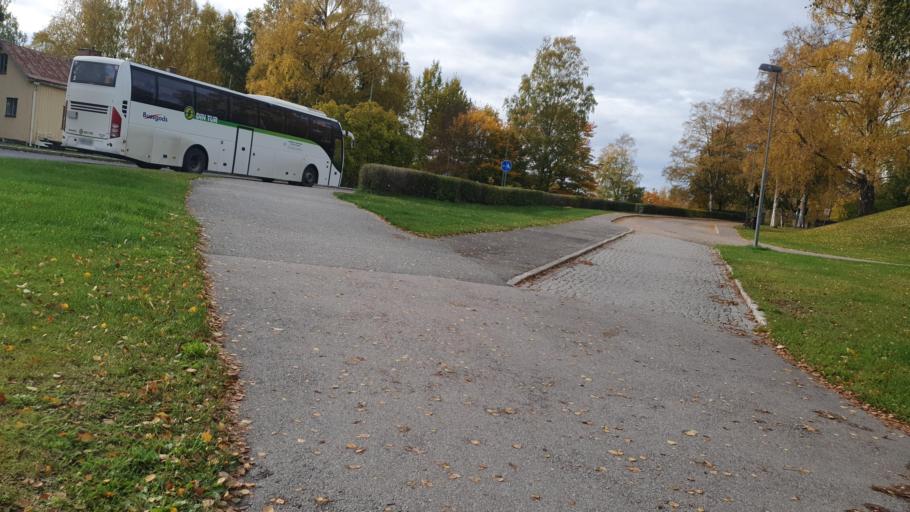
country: SE
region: Vaesternorrland
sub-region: Sundsvalls Kommun
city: Sundsvall
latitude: 62.3943
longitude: 17.2766
